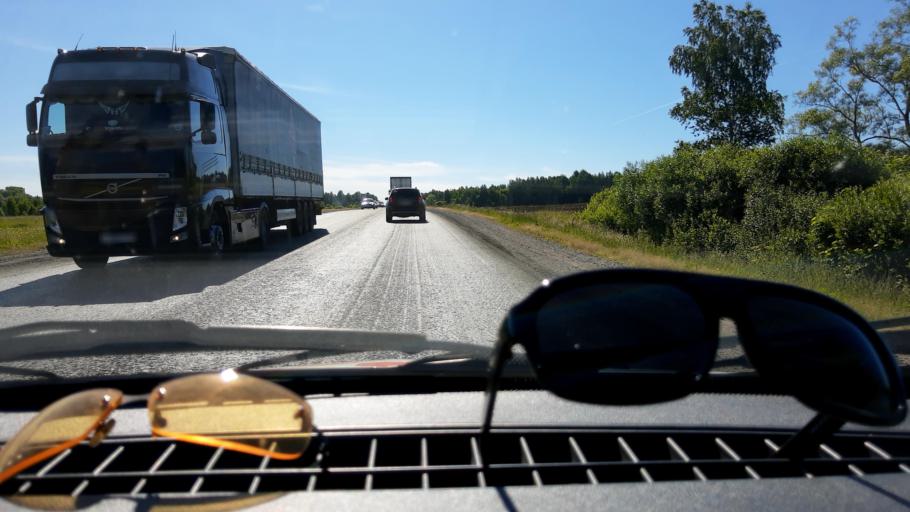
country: RU
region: Bashkortostan
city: Kudeyevskiy
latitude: 54.8164
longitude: 56.7033
